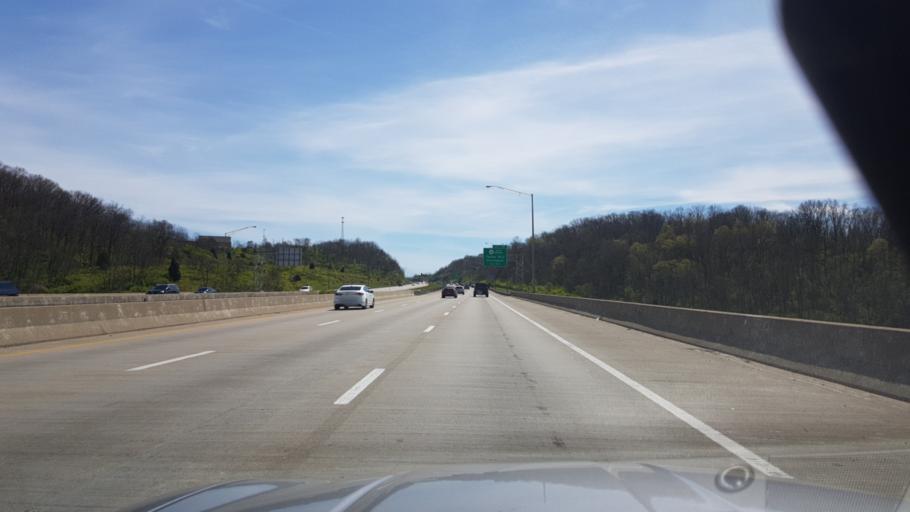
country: US
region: Kentucky
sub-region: Kenton County
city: Fort Wright
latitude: 39.0270
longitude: -84.5311
